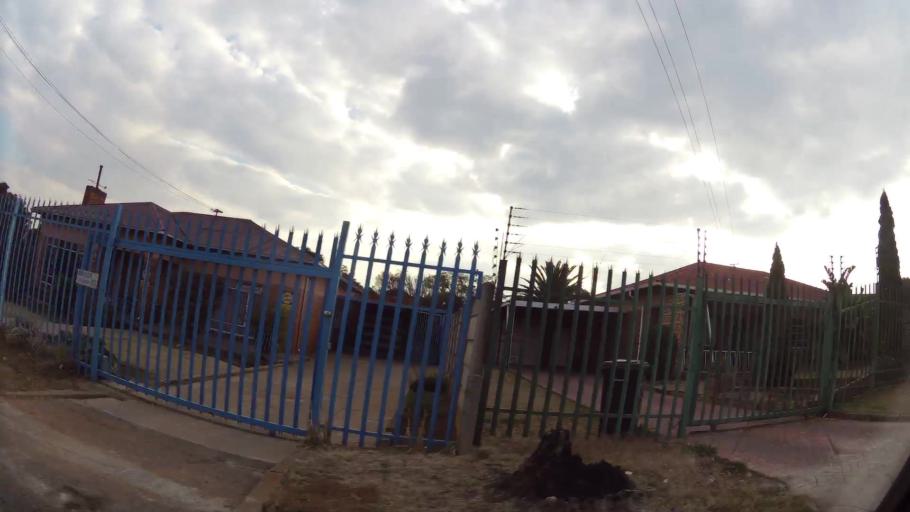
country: ZA
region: Gauteng
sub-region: Ekurhuleni Metropolitan Municipality
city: Germiston
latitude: -26.2419
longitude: 28.2020
